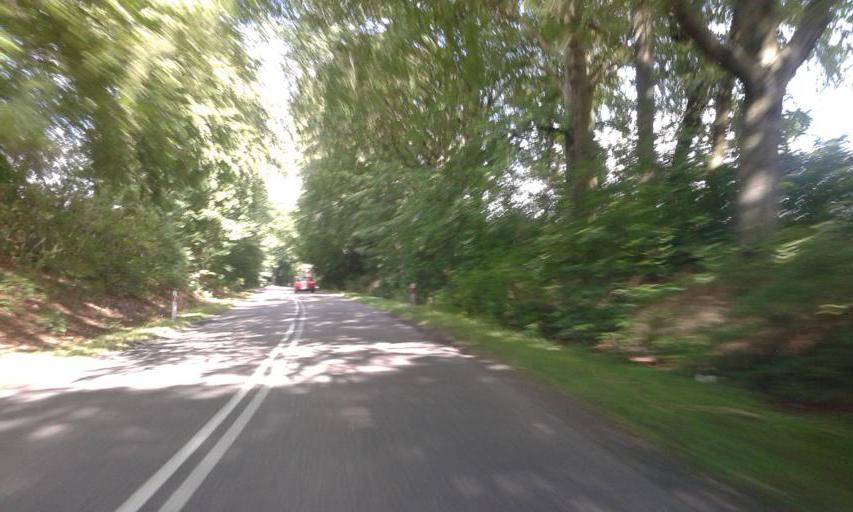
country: PL
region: West Pomeranian Voivodeship
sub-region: Powiat slawienski
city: Slawno
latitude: 54.2686
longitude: 16.6768
